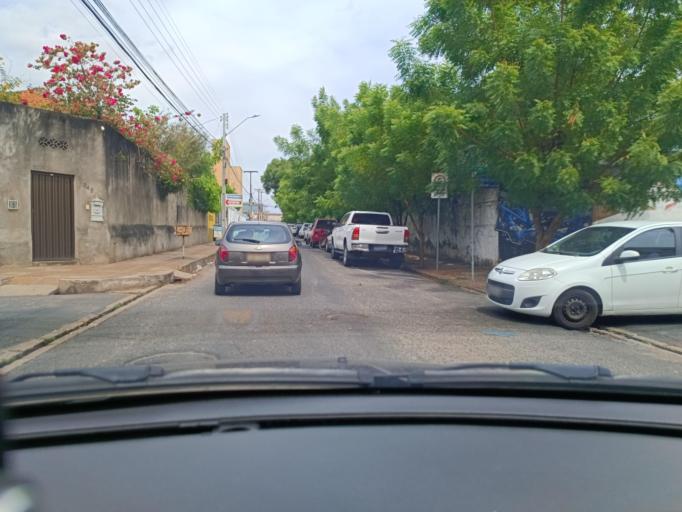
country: BR
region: Piaui
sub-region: Teresina
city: Teresina
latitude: -5.0897
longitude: -42.8076
